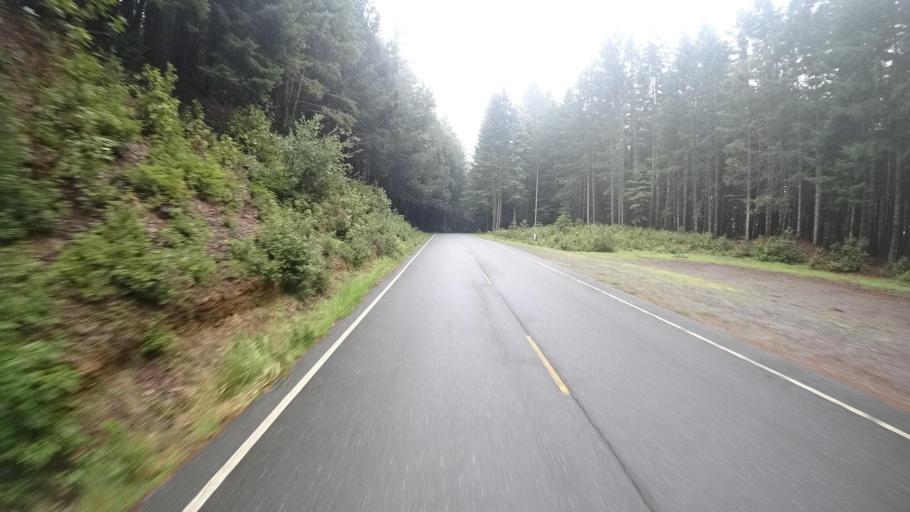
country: US
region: California
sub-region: Humboldt County
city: Westhaven-Moonstone
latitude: 41.1992
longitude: -123.9429
